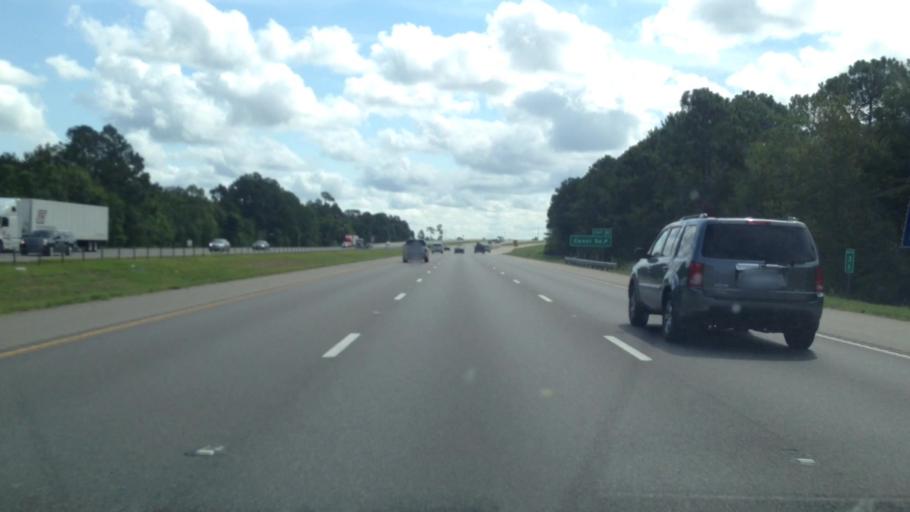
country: US
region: Mississippi
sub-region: Harrison County
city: West Gulfport
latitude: 30.4227
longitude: -89.1474
